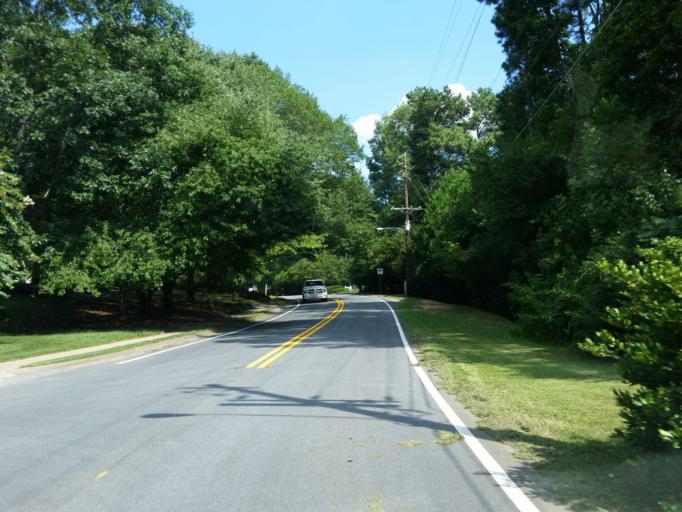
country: US
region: Georgia
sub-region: Cherokee County
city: Woodstock
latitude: 34.0304
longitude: -84.4586
